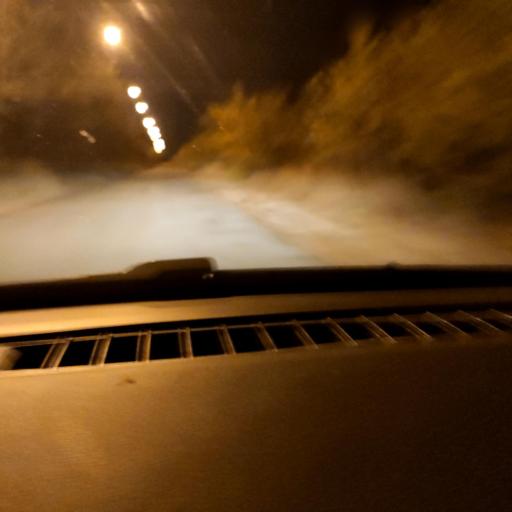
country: RU
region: Voronezj
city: Pridonskoy
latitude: 51.6838
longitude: 39.0958
